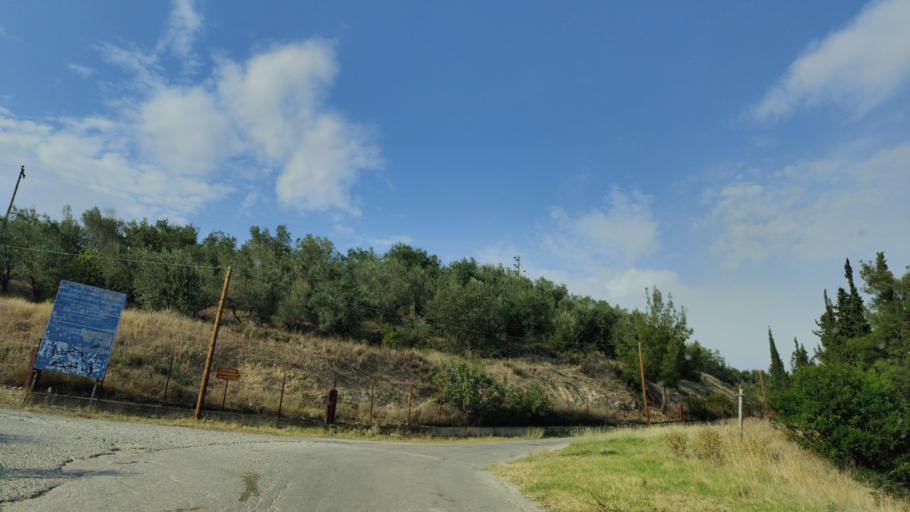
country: GR
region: Central Macedonia
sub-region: Nomos Serron
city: Sidirokastro
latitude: 41.2342
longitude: 23.3987
